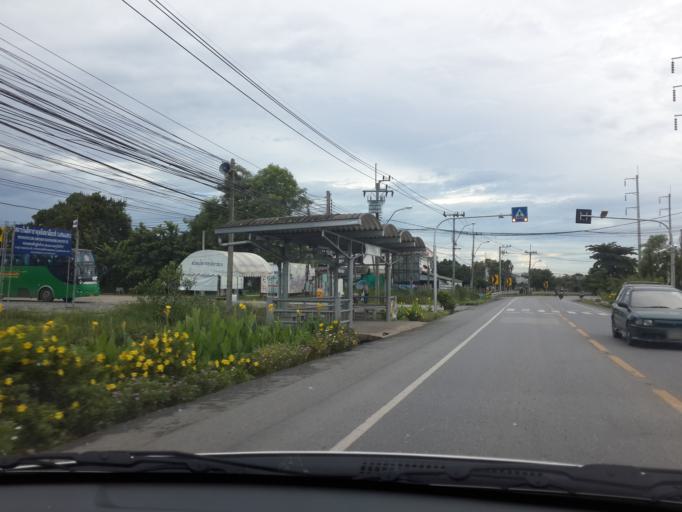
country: TH
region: Bangkok
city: Khlong Sam Wa
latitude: 13.8253
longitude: 100.7521
